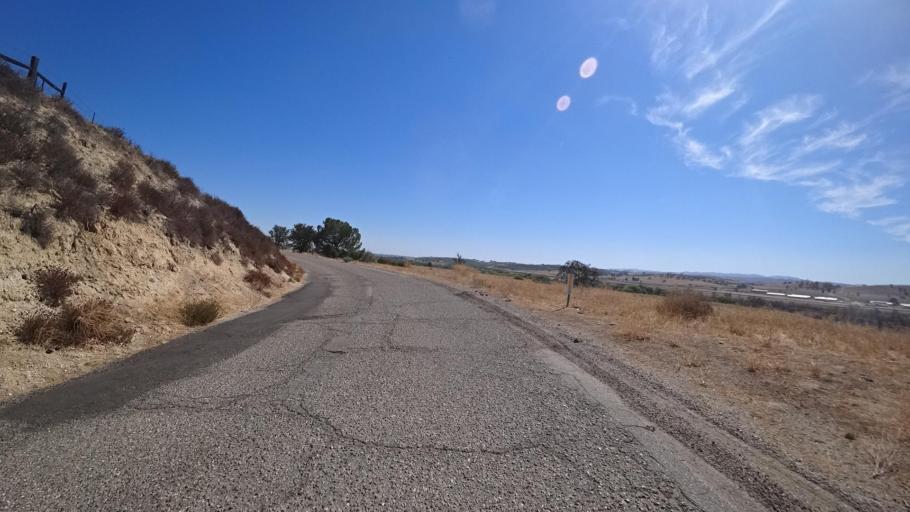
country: US
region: California
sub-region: San Luis Obispo County
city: San Miguel
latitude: 35.7901
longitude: -120.7187
